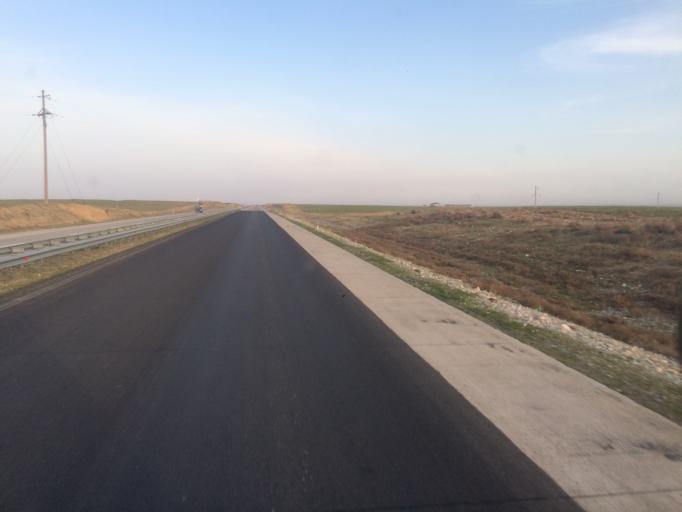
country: KZ
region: Ongtustik Qazaqstan
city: Temirlanovka
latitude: 42.5182
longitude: 69.4162
